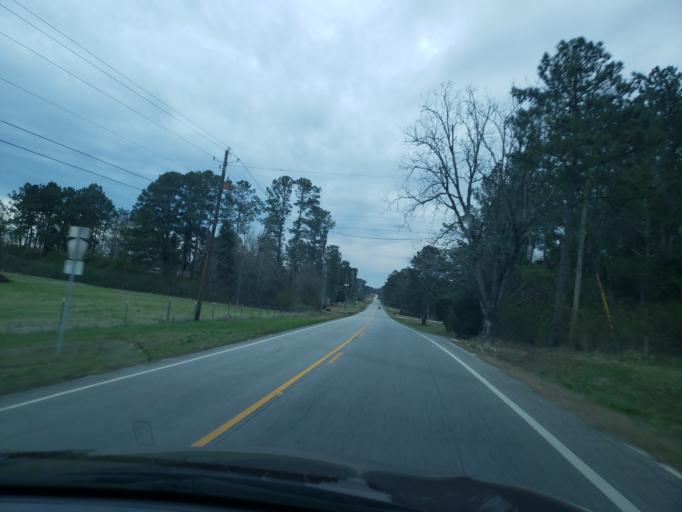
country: US
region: Alabama
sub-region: Chambers County
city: Lafayette
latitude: 32.9939
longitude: -85.3809
